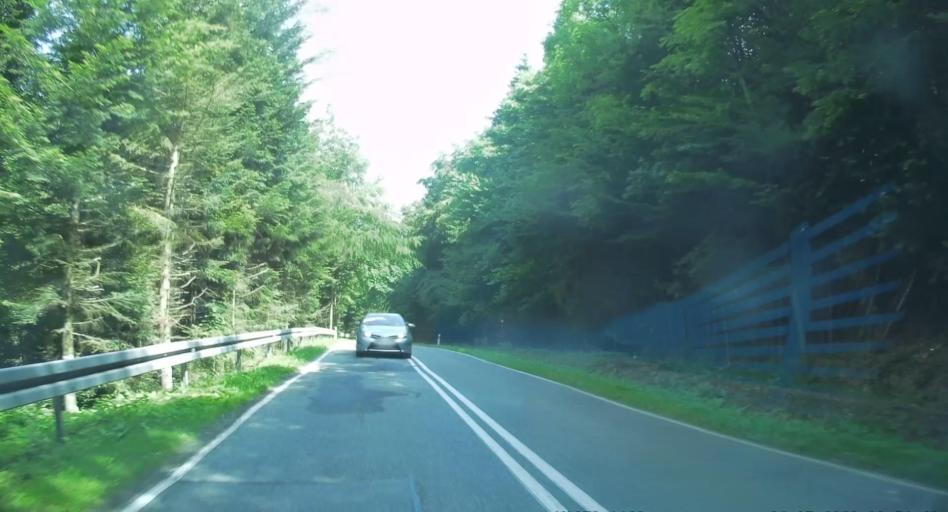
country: PL
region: Lesser Poland Voivodeship
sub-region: Powiat tarnowski
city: Zakliczyn
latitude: 49.7744
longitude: 20.7739
